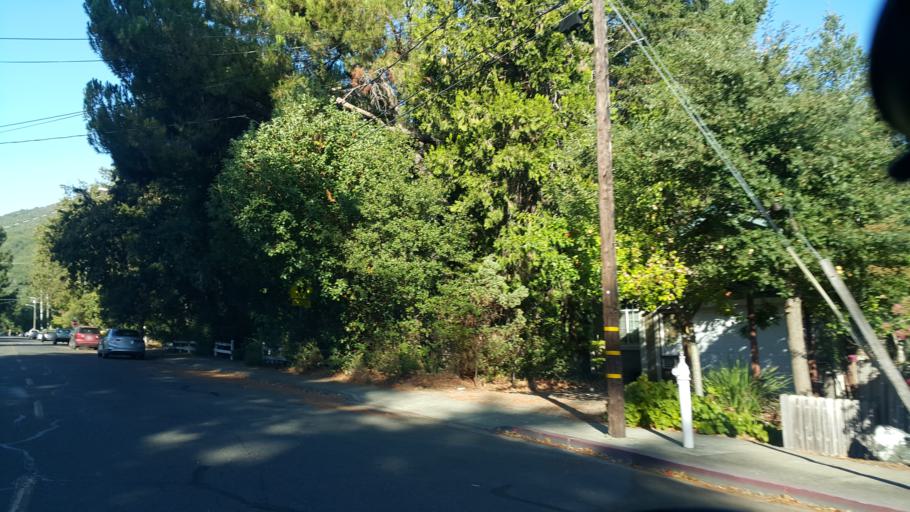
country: US
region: California
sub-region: Mendocino County
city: Ukiah
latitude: 39.1546
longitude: -123.2146
